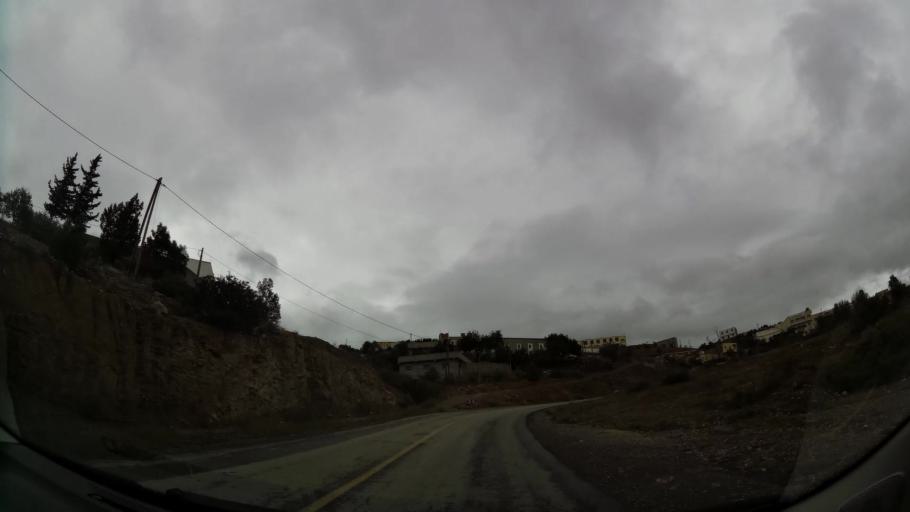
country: MA
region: Taza-Al Hoceima-Taounate
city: Imzourene
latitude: 34.9522
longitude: -3.8082
